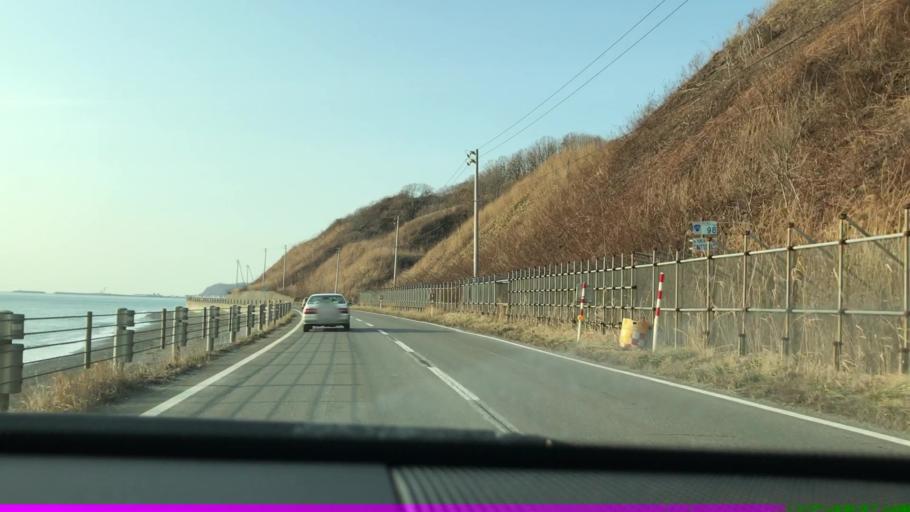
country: JP
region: Hokkaido
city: Shizunai-furukawacho
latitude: 42.2361
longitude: 142.5982
